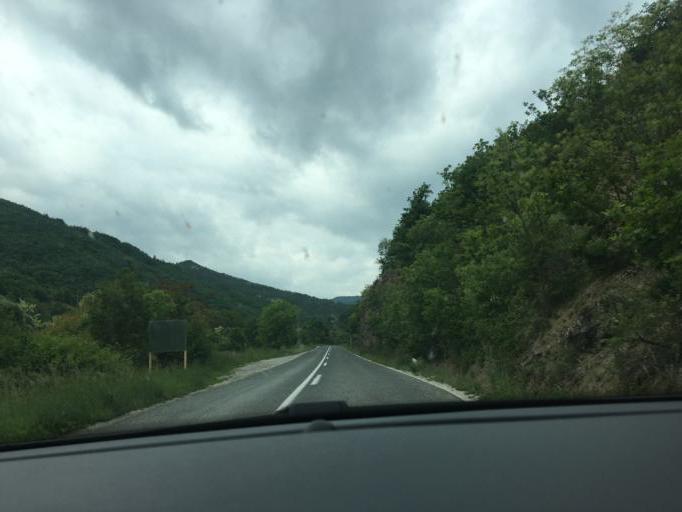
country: MK
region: Ohrid
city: Kosel
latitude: 41.2019
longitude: 20.8930
